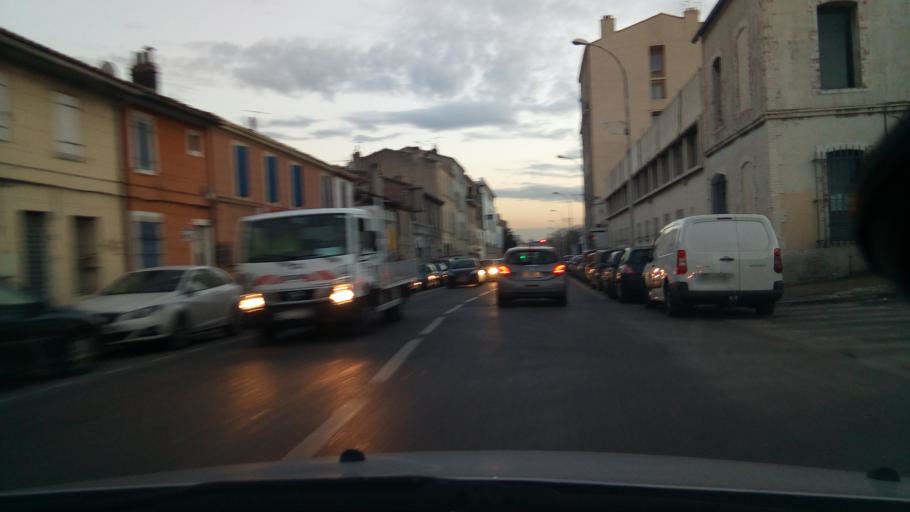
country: FR
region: Provence-Alpes-Cote d'Azur
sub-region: Departement des Bouches-du-Rhone
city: Marseille 14
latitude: 43.3269
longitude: 5.3661
